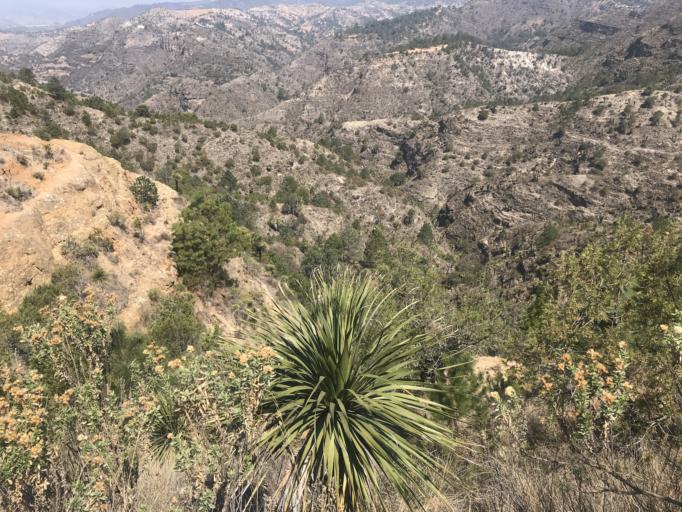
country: MX
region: Puebla
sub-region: Zautla
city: San Andres Yahuitlalpan
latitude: 19.6778
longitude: -97.8094
